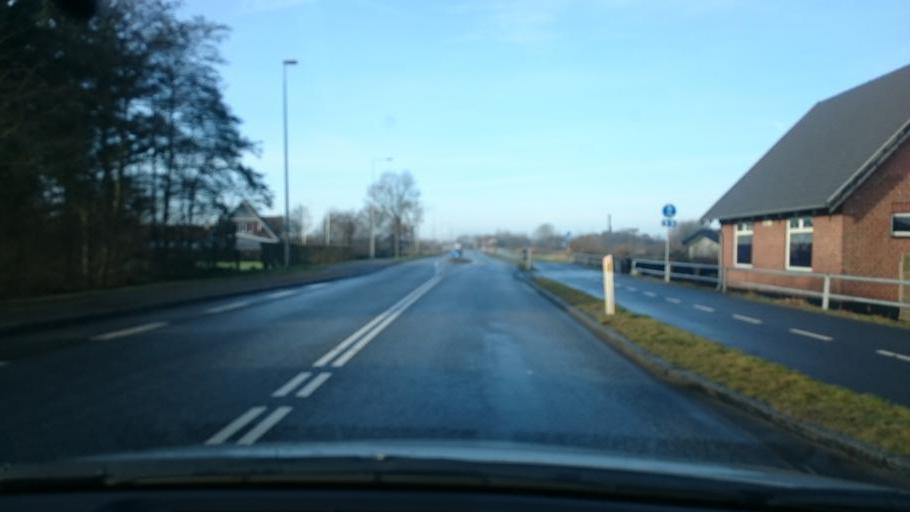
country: DK
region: South Denmark
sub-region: Esbjerg Kommune
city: Ribe
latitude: 55.3184
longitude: 8.7706
